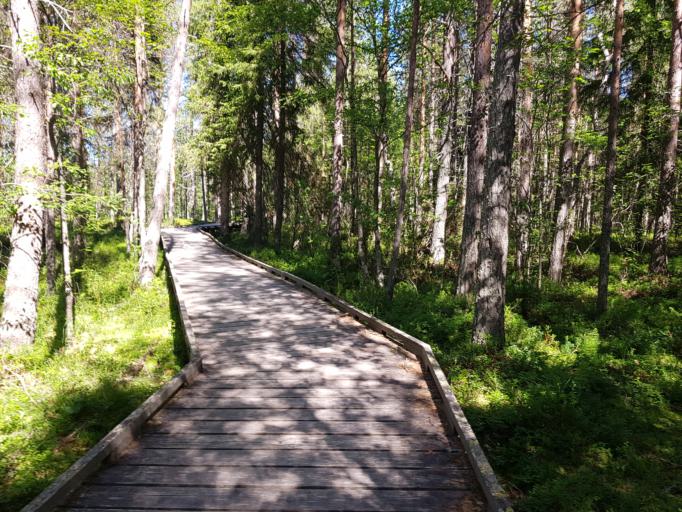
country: FI
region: Kainuu
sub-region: Kehys-Kainuu
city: Kuhmo
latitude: 64.1942
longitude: 29.5943
